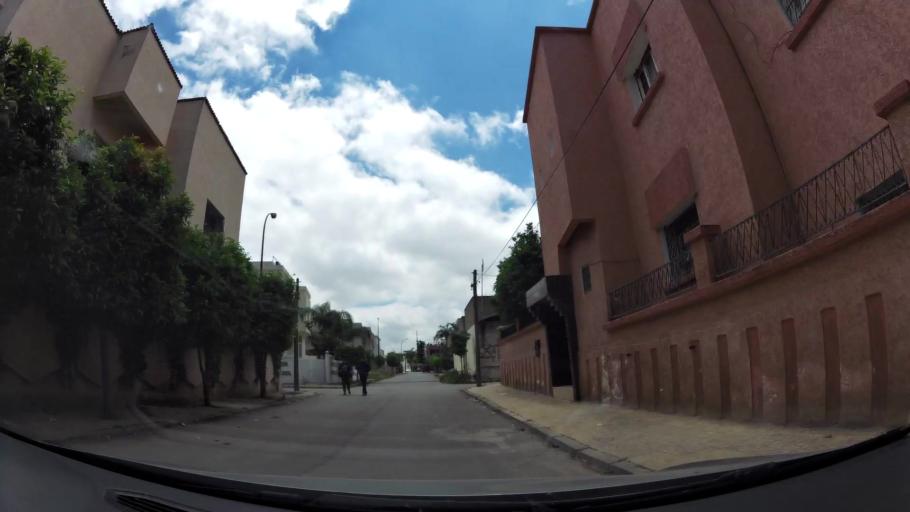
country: MA
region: Fes-Boulemane
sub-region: Fes
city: Fes
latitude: 34.0374
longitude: -5.0205
